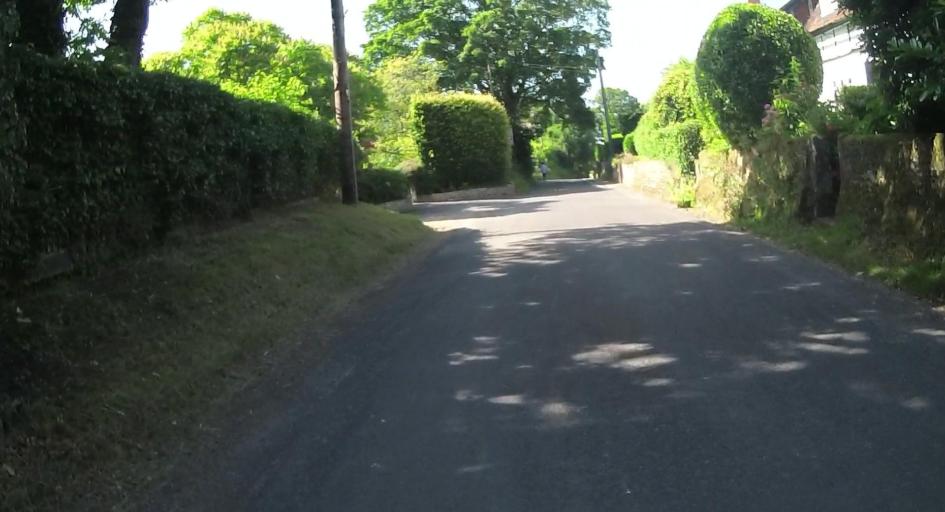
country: GB
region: England
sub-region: Hampshire
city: Kingsley
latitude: 51.1630
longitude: -0.8982
